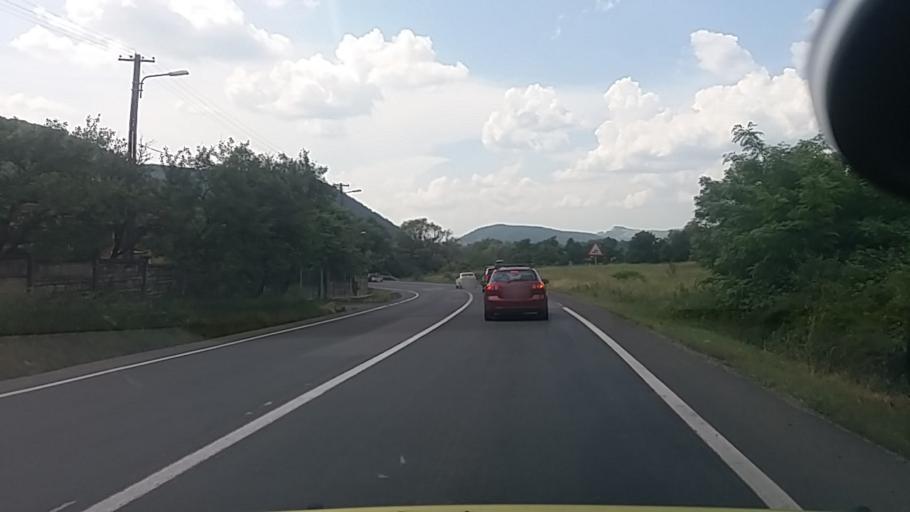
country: RO
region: Hunedoara
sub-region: Comuna Branisca
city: Branisca
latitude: 45.9048
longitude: 22.7856
